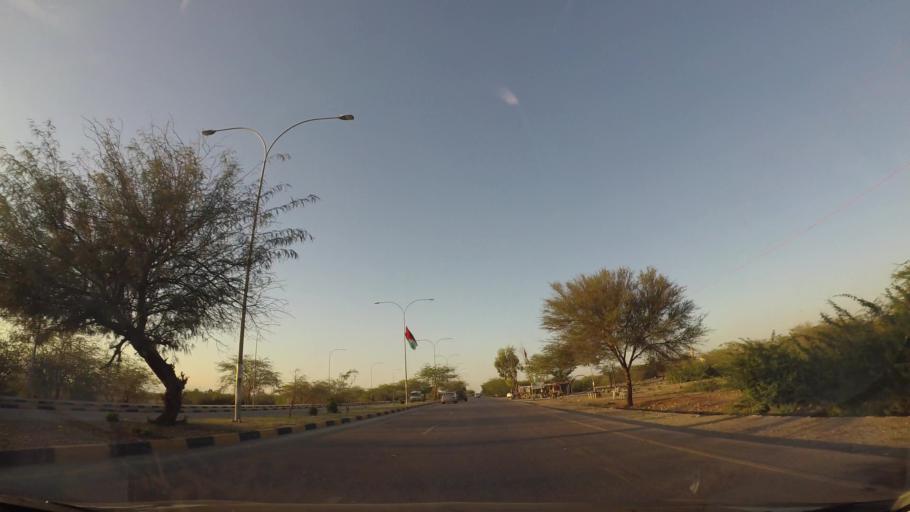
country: PS
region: West Bank
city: Jericho
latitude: 31.7715
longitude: 35.5926
